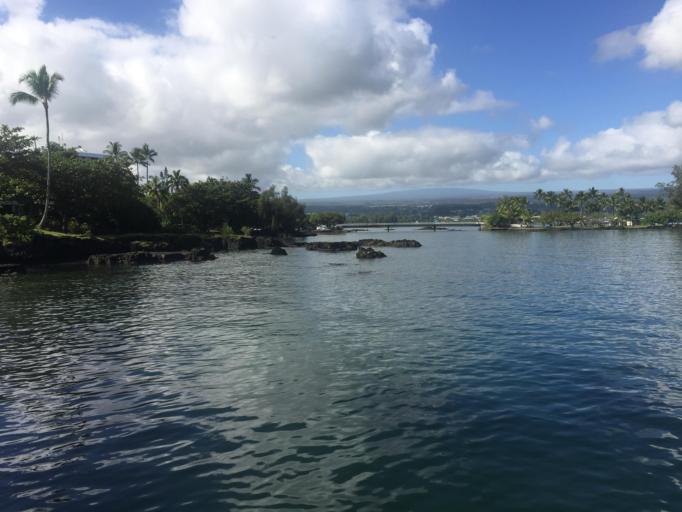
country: US
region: Hawaii
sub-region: Hawaii County
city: Hilo
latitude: 19.7302
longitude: -155.0655
